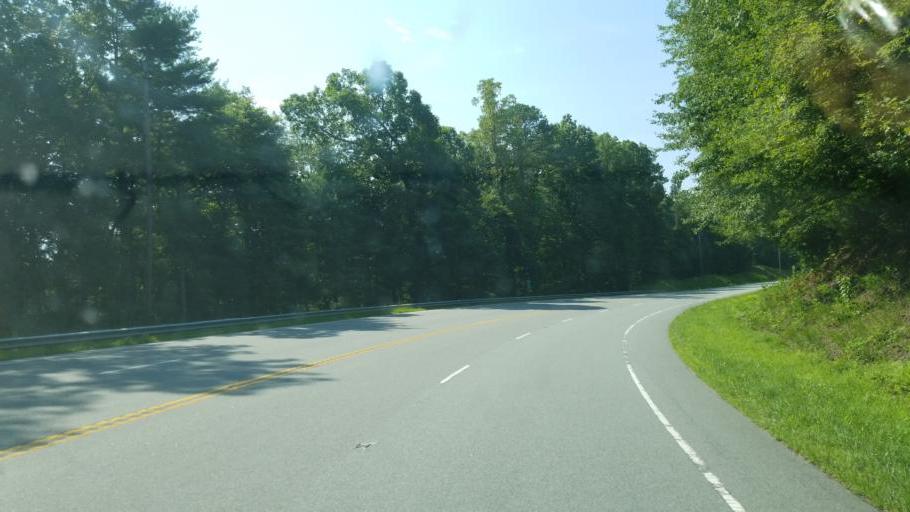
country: US
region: North Carolina
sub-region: Burke County
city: Glen Alpine
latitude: 35.8924
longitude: -81.8030
